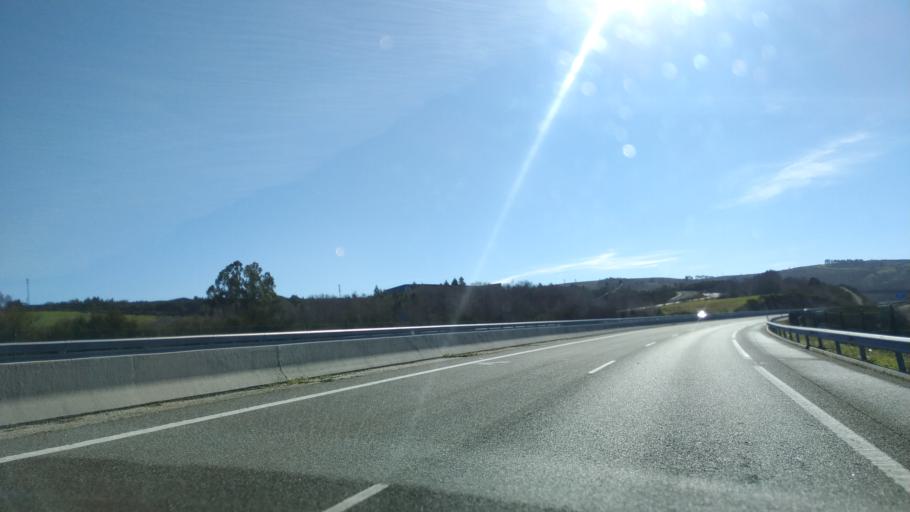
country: ES
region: Galicia
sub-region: Provincia de Pontevedra
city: Dozon
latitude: 42.5772
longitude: -8.0625
